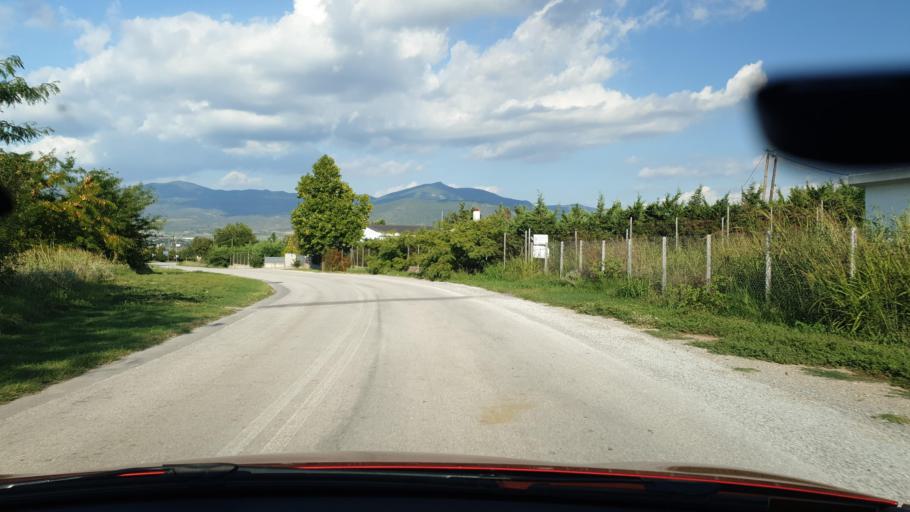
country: GR
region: Central Macedonia
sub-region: Nomos Thessalonikis
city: Souroti
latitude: 40.4745
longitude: 23.0959
